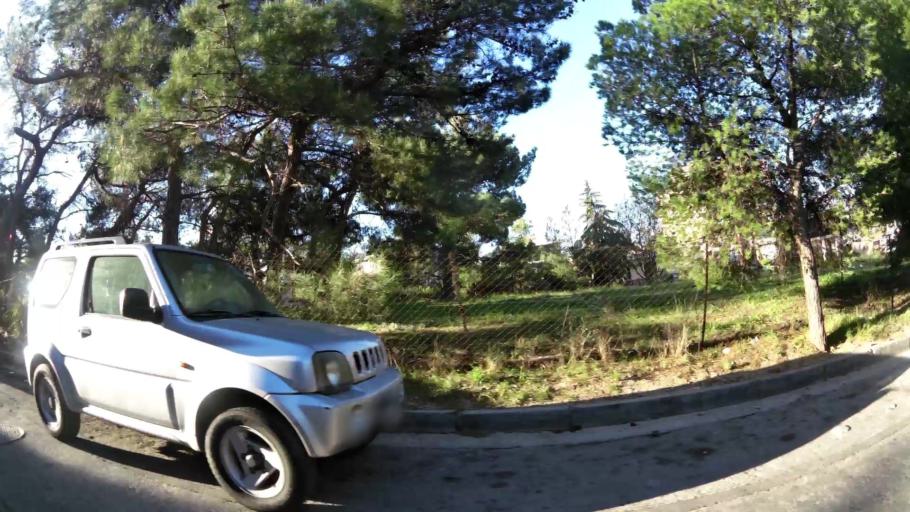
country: GR
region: Attica
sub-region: Nomarchia Athinas
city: Lykovrysi
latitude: 38.0614
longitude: 23.7776
